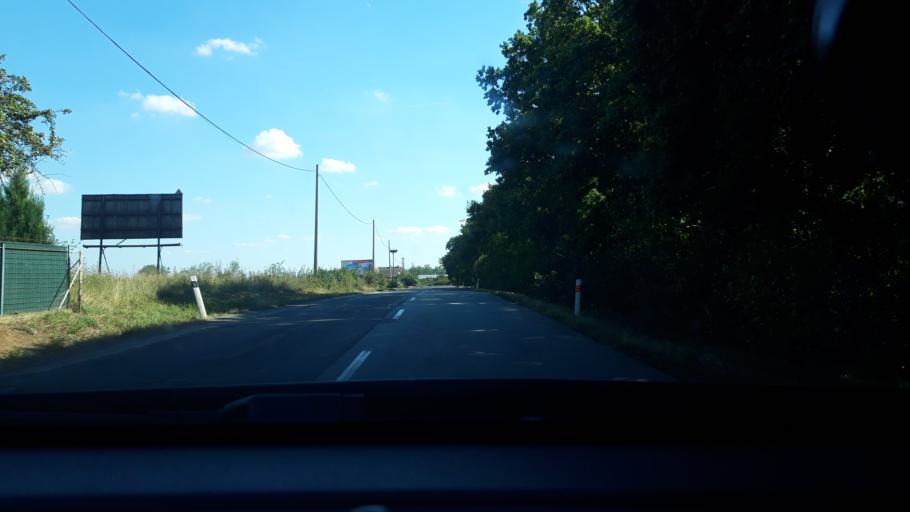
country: SK
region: Kosicky
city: Secovce
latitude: 48.6261
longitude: 21.5871
